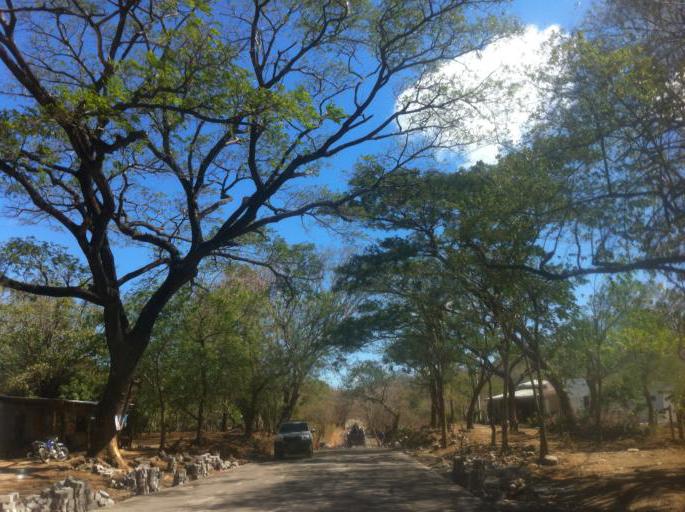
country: NI
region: Rivas
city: Tola
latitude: 11.3994
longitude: -85.9943
